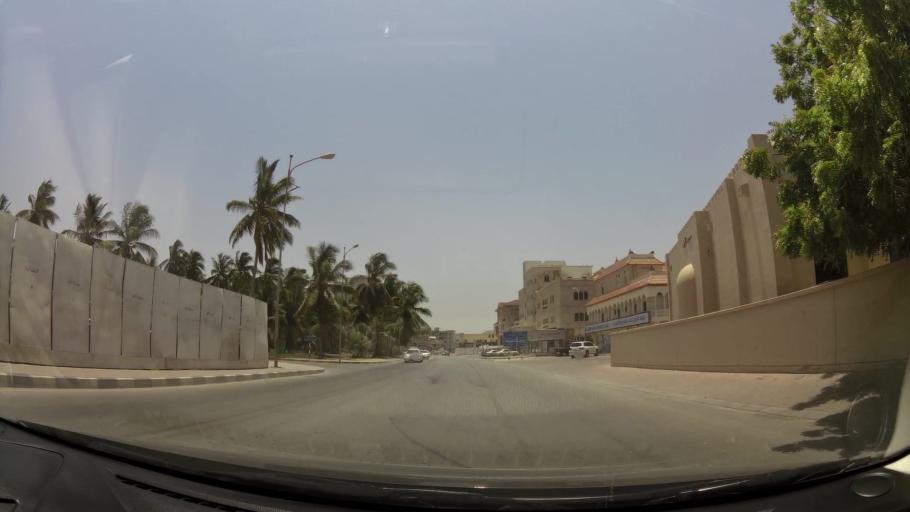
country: OM
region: Zufar
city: Salalah
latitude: 17.0127
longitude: 54.1064
